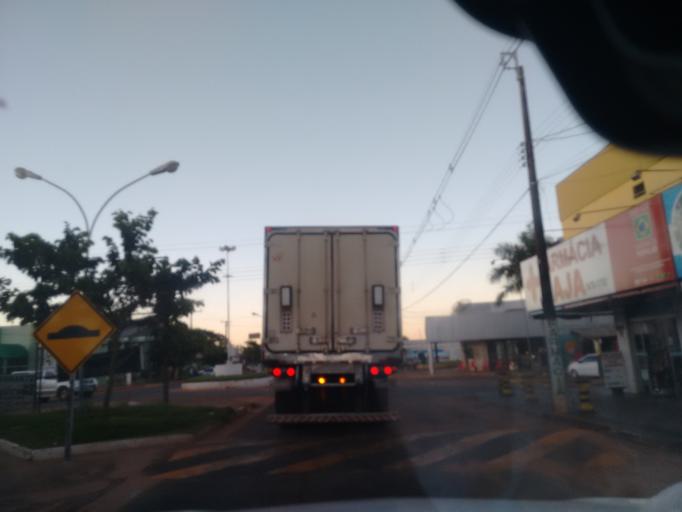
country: BR
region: Mato Grosso do Sul
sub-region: Eldorado
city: Eldorado
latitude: -23.4756
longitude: -54.1878
